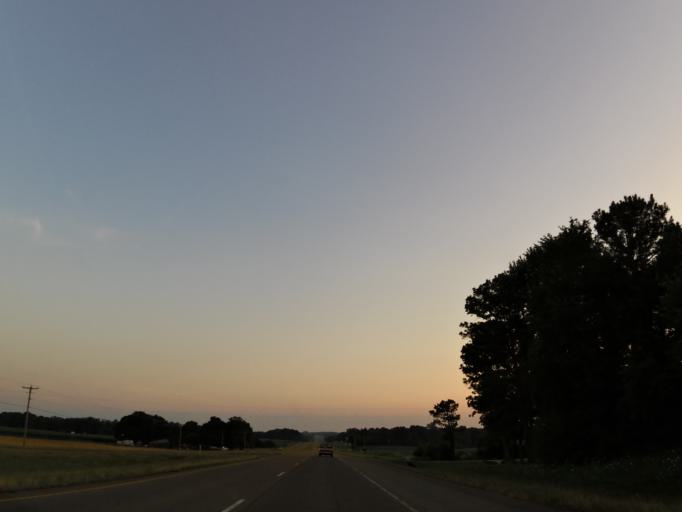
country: US
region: Tennessee
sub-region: Carroll County
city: McKenzie
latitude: 36.1690
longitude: -88.4511
